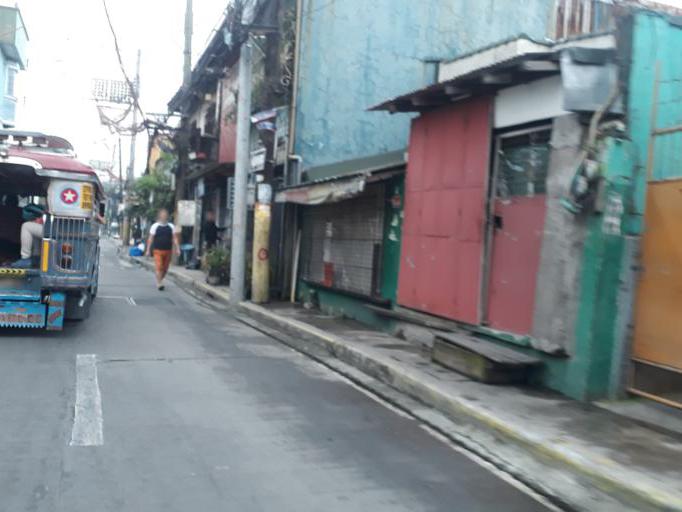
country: PH
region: Calabarzon
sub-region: Province of Rizal
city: Navotas
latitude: 14.6572
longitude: 120.9463
